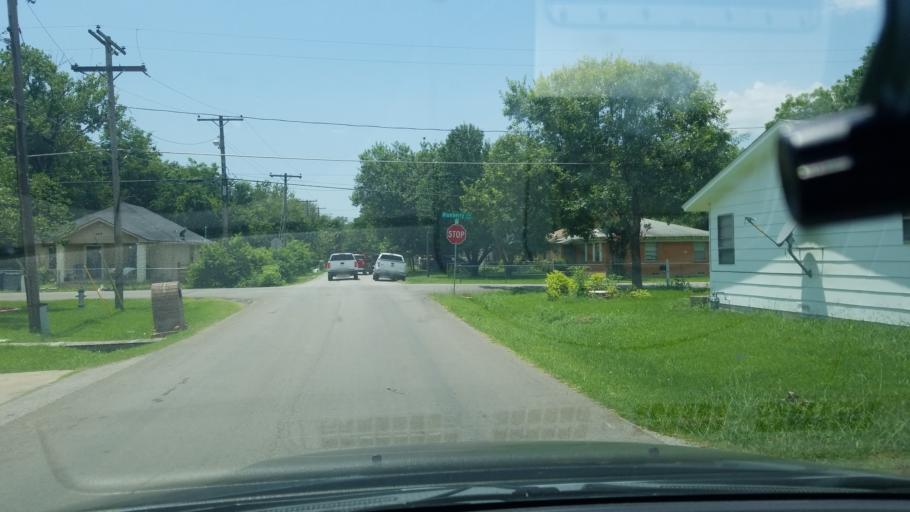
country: US
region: Texas
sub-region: Dallas County
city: Balch Springs
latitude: 32.7292
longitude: -96.6678
